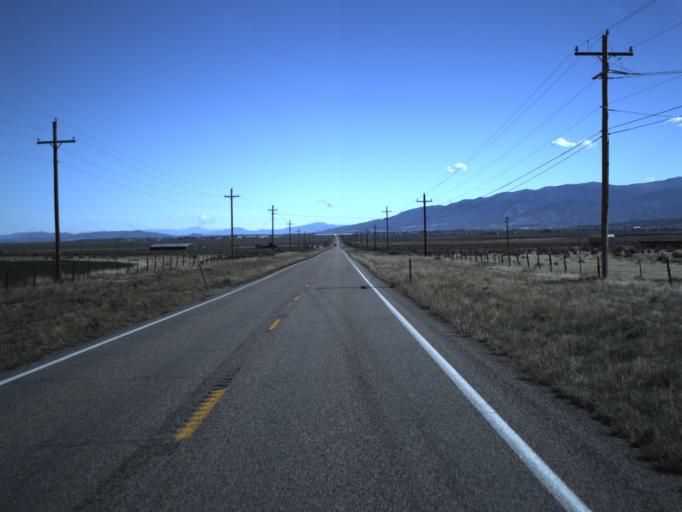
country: US
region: Utah
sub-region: Iron County
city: Cedar City
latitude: 37.6557
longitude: -113.2224
